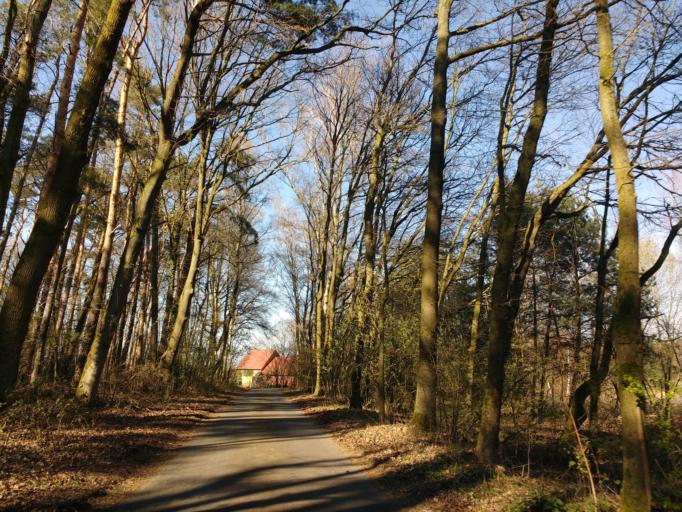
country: DE
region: North Rhine-Westphalia
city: Geseke
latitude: 51.7096
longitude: 8.5041
